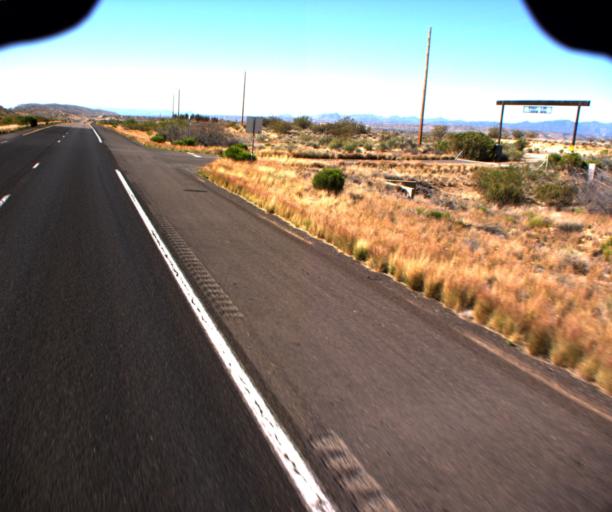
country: US
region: Arizona
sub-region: Mohave County
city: Kingman
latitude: 35.0292
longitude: -113.6650
